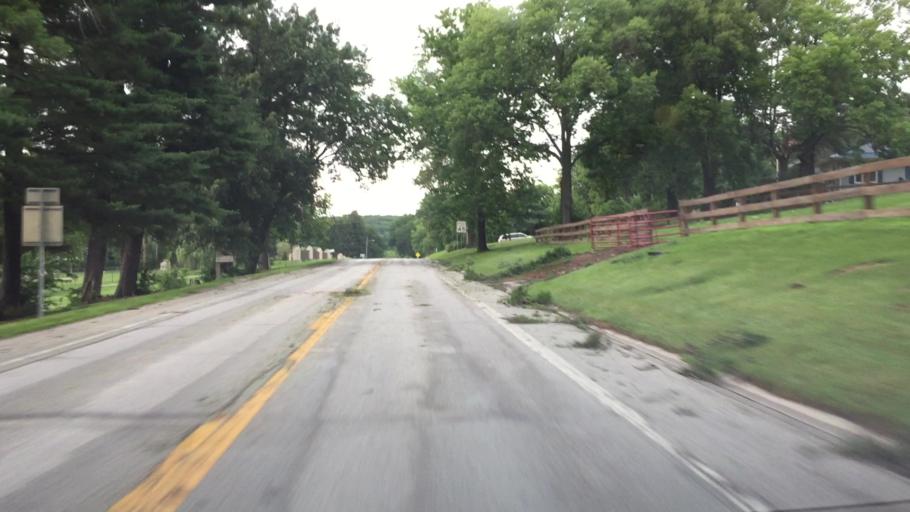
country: US
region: Illinois
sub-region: Hancock County
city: Hamilton
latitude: 40.4002
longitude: -91.3518
